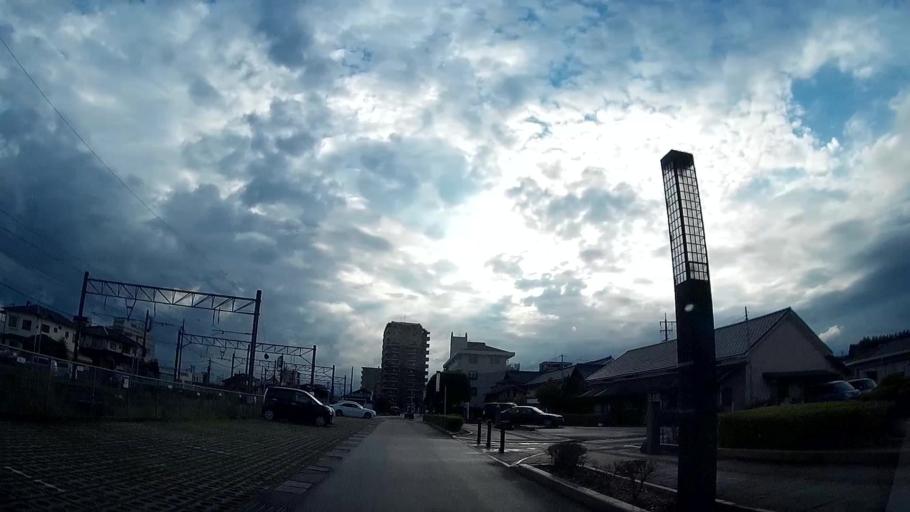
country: JP
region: Kumamoto
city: Ozu
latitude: 32.8777
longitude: 130.8676
